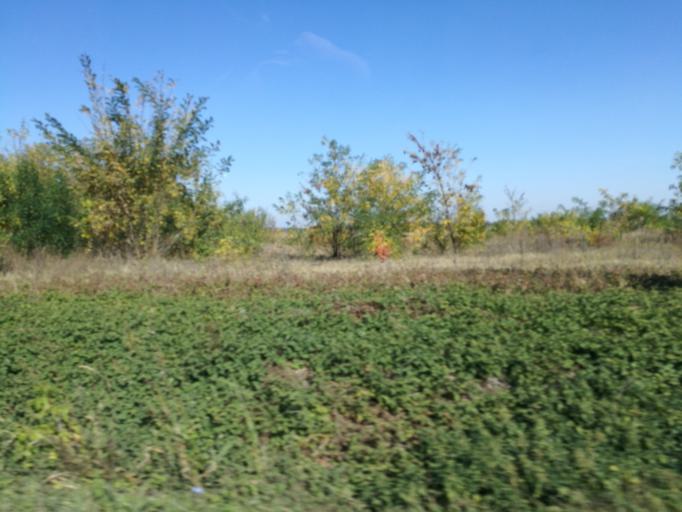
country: RO
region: Ilfov
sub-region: Comuna Dragomiresti-Vale
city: Dragomiresti-Vale
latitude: 44.4696
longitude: 25.9197
